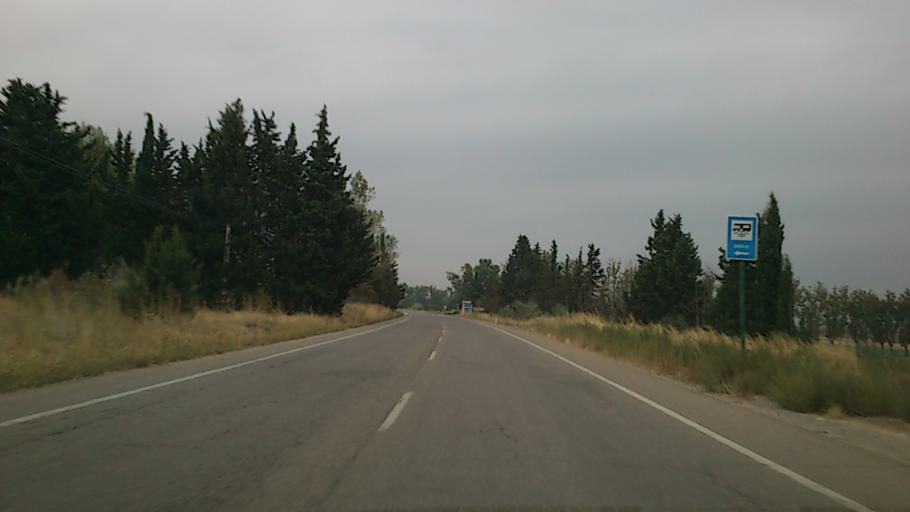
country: ES
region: Aragon
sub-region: Provincia de Zaragoza
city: Villanueva de Gallego
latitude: 41.7348
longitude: -0.8087
